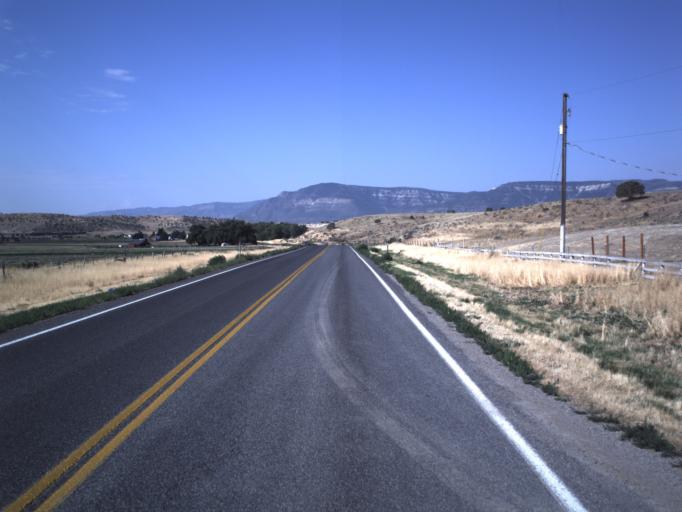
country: US
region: Utah
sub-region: Sanpete County
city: Moroni
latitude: 39.5386
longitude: -111.5366
